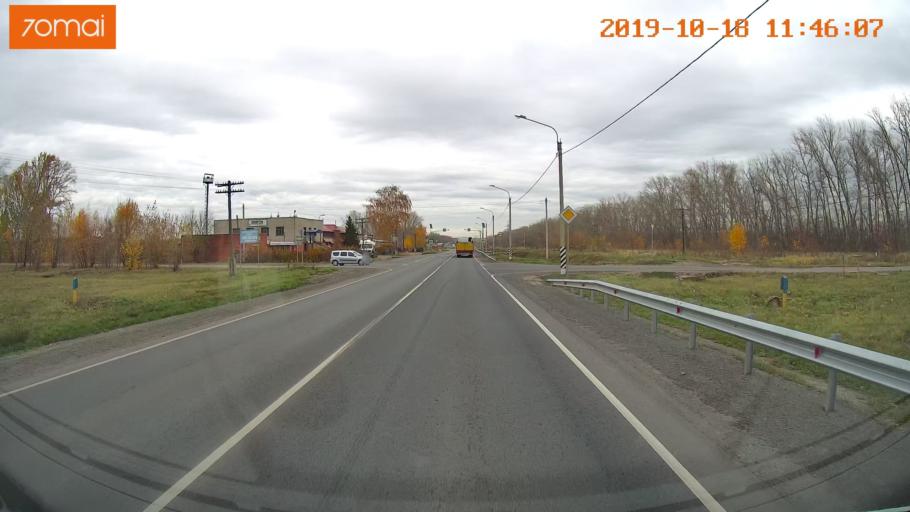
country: RU
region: Rjazan
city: Mikhaylov
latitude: 54.2168
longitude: 38.9793
